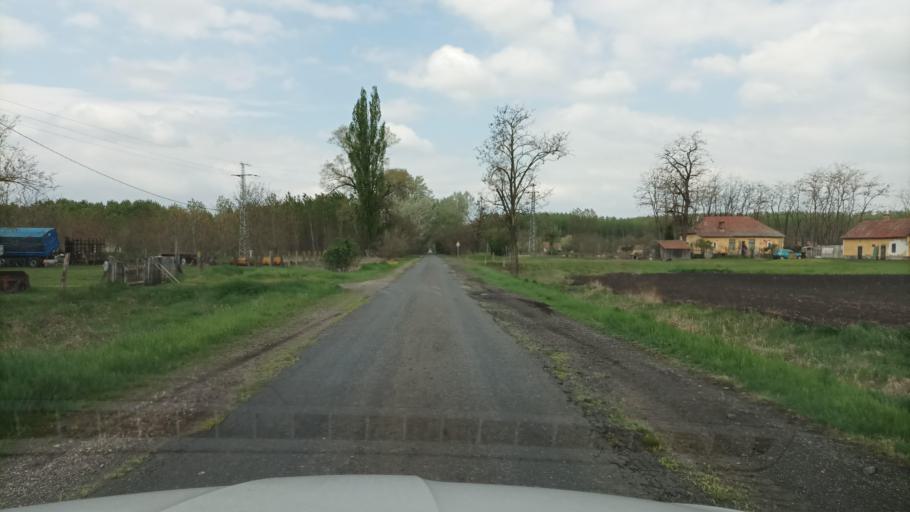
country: HU
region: Pest
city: Kocser
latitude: 47.0443
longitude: 19.9311
